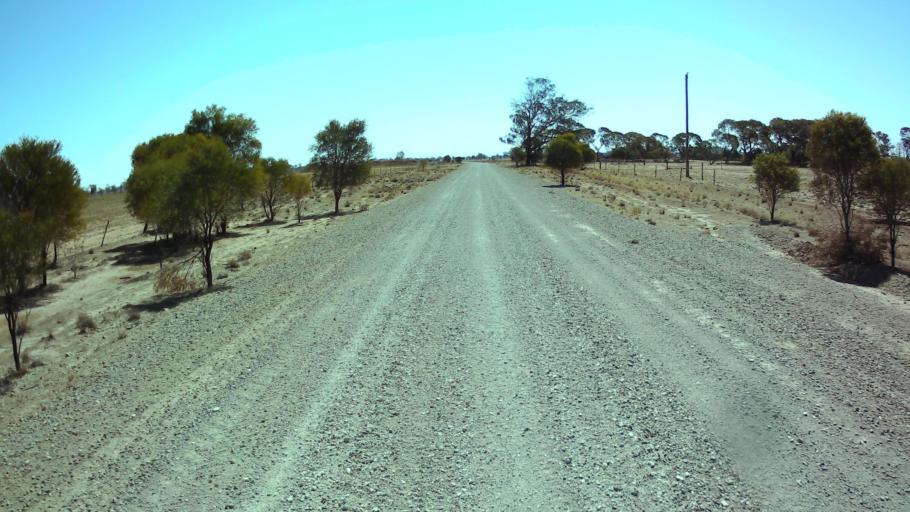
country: AU
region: New South Wales
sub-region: Forbes
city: Forbes
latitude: -33.7454
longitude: 147.7382
